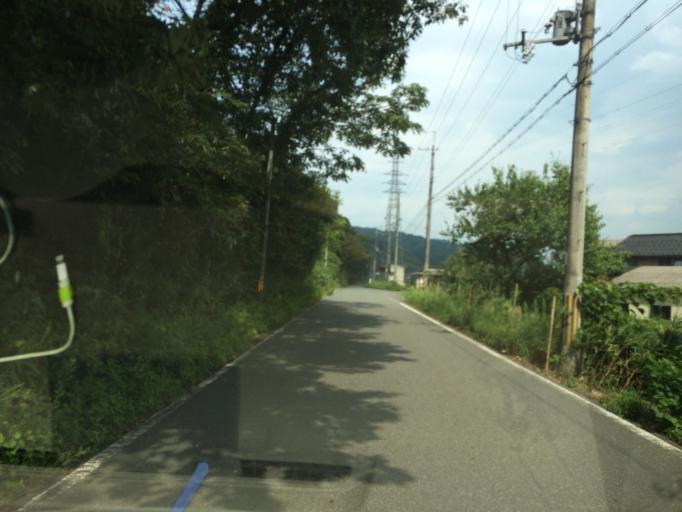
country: JP
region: Hyogo
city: Toyooka
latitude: 35.4879
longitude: 134.7800
